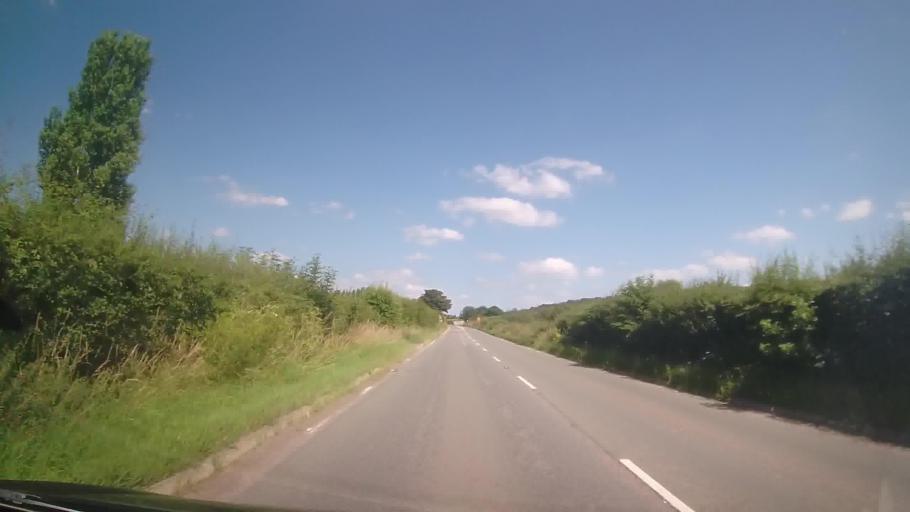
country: GB
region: England
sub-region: Herefordshire
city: Withington
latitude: 52.0592
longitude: -2.6134
